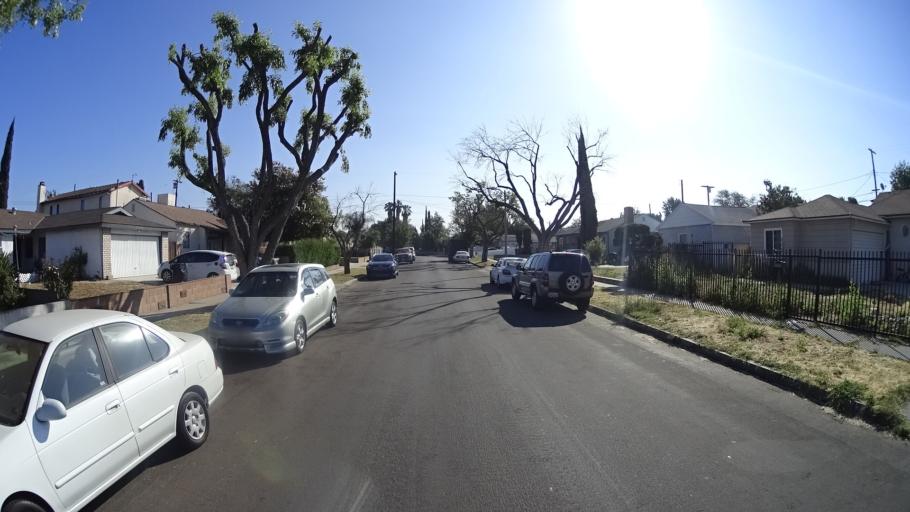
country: US
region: California
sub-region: Los Angeles County
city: Van Nuys
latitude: 34.2292
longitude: -118.4276
